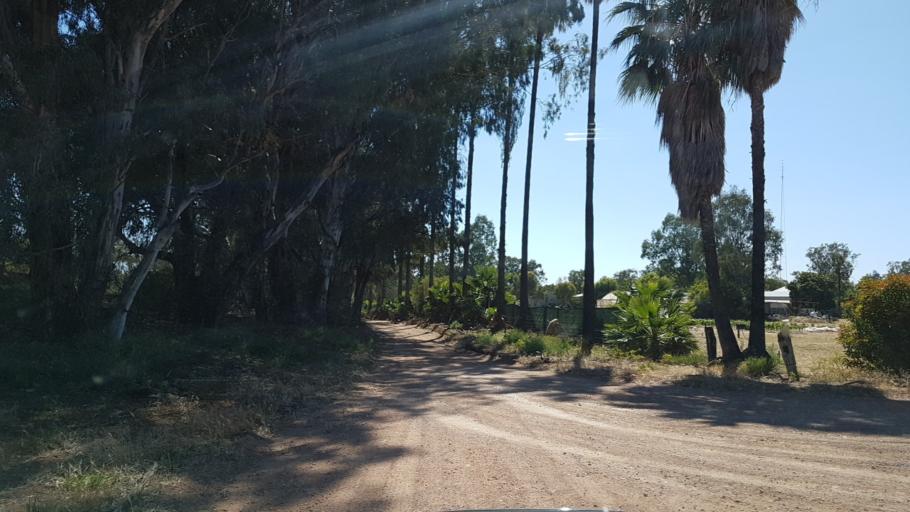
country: AU
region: South Australia
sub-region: Loxton Waikerie
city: Waikerie
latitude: -34.1642
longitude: 140.0315
